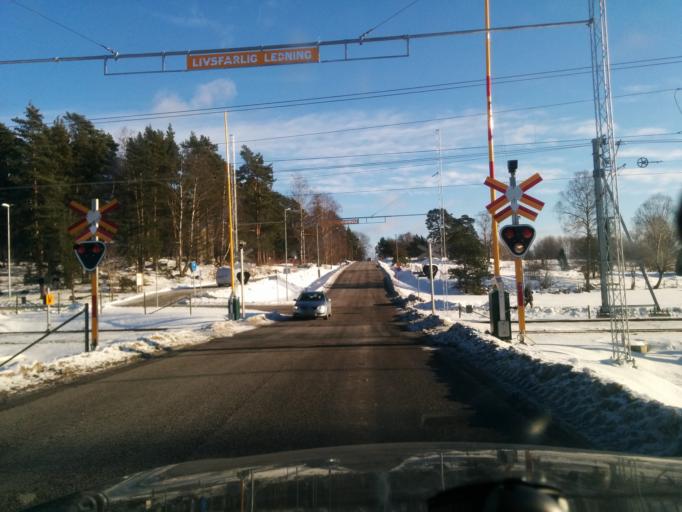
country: SE
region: Stockholm
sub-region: Vallentuna Kommun
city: Vallentuna
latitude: 59.4903
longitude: 18.0628
